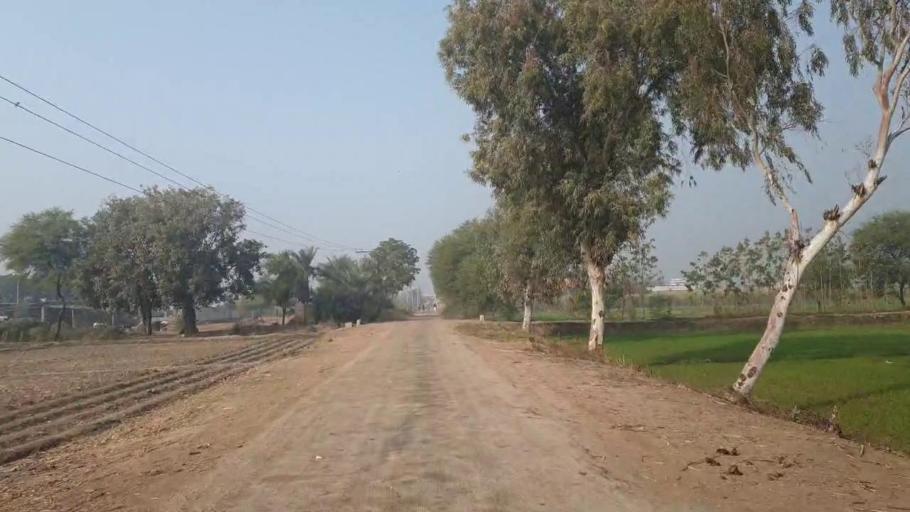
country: PK
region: Sindh
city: Tando Adam
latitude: 25.8014
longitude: 68.6169
